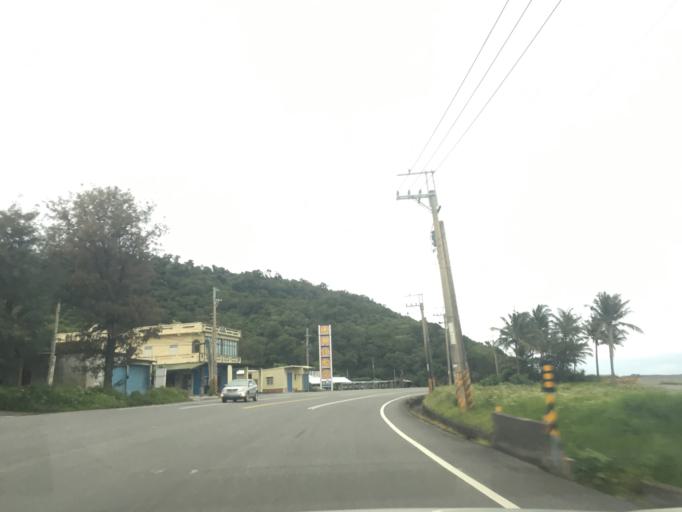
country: TW
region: Taiwan
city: Hengchun
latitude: 22.3301
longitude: 120.8923
